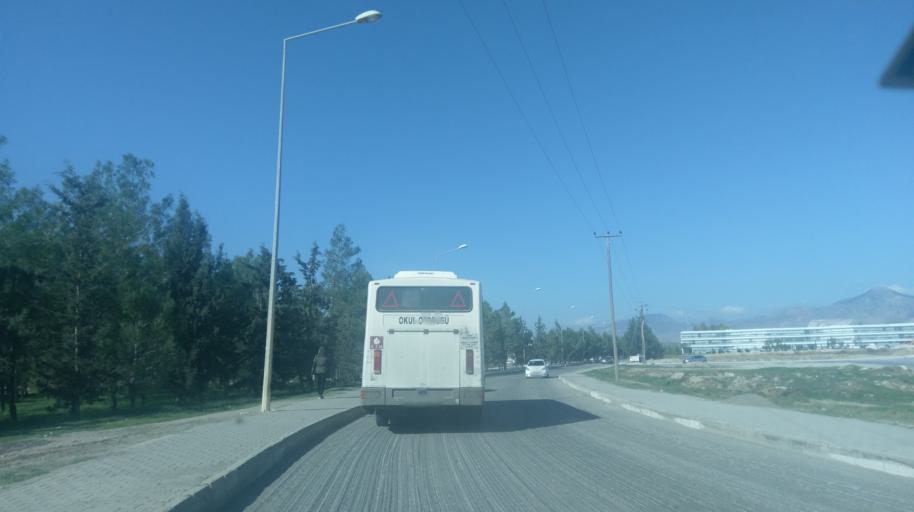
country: CY
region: Lefkosia
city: Nicosia
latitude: 35.2184
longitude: 33.4205
